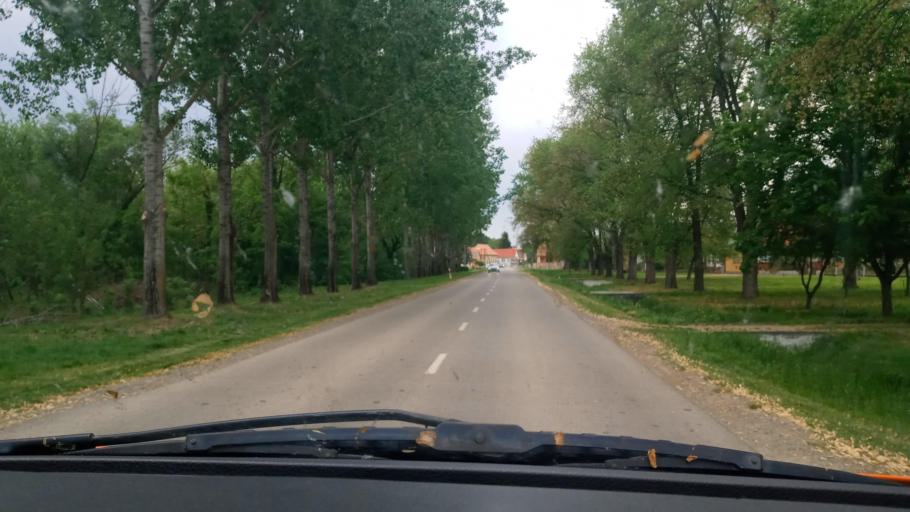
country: HU
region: Baranya
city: Villany
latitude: 45.8439
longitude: 18.4890
